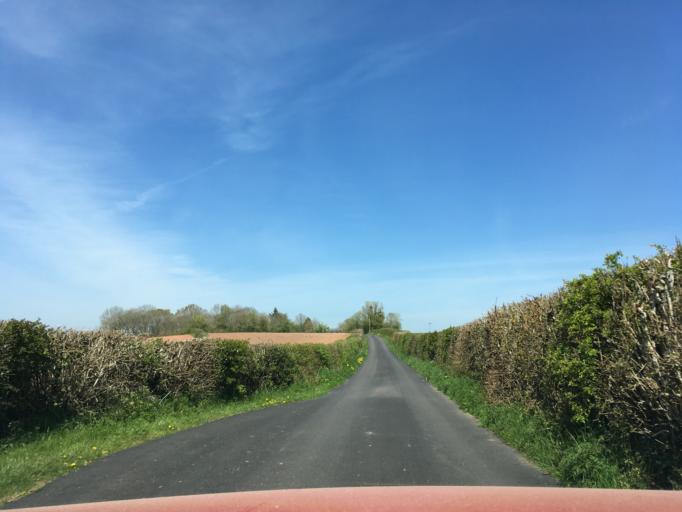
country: GB
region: Wales
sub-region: Monmouthshire
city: Llangwm
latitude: 51.7616
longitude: -2.8271
